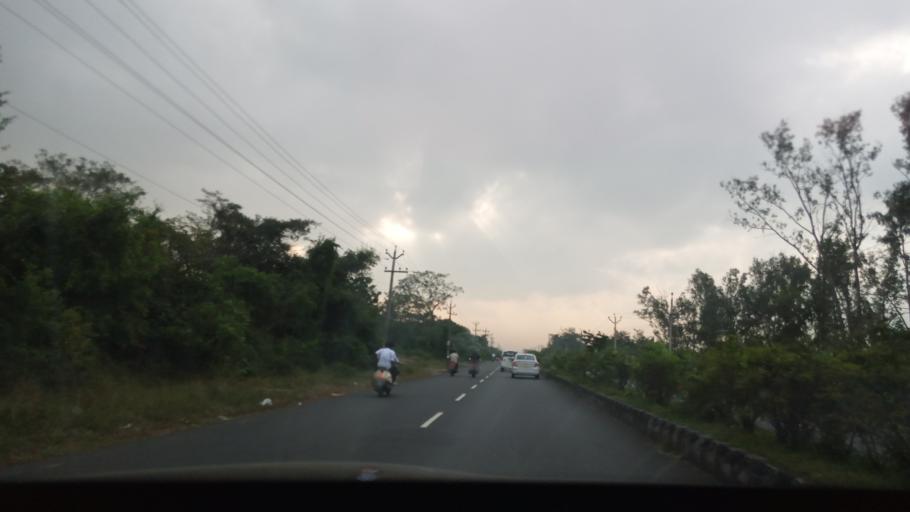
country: IN
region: Tamil Nadu
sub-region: Kancheepuram
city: Vengavasal
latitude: 12.8177
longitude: 80.1760
